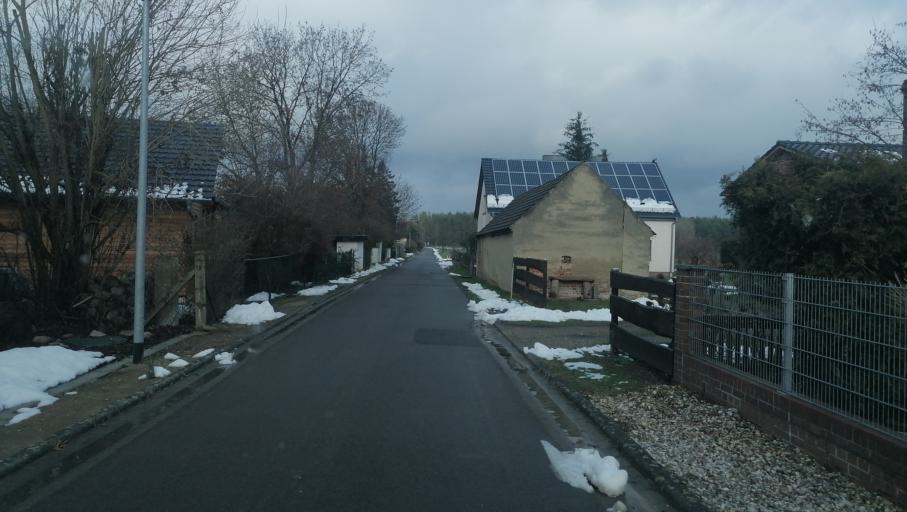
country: DE
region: Brandenburg
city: Cottbus
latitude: 51.6817
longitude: 14.3385
